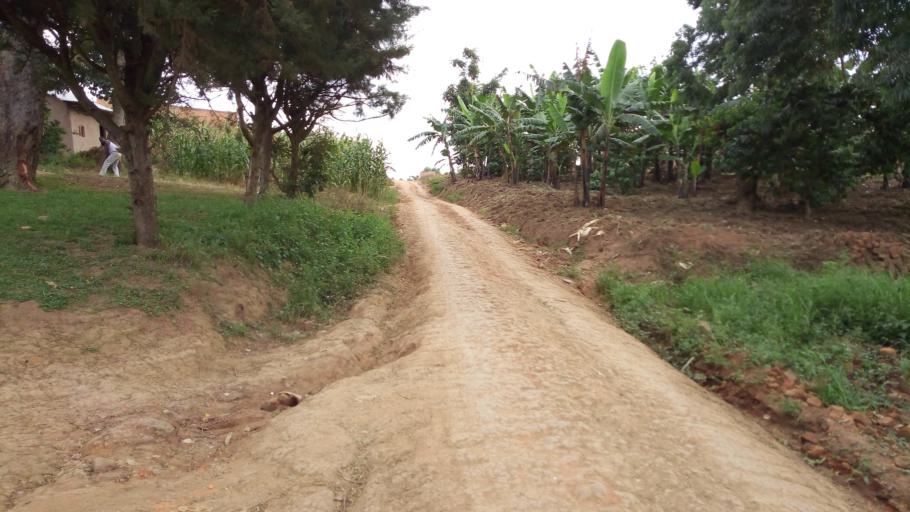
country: UG
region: Central Region
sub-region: Kiboga District
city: Kiboga
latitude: 0.7398
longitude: 31.7258
